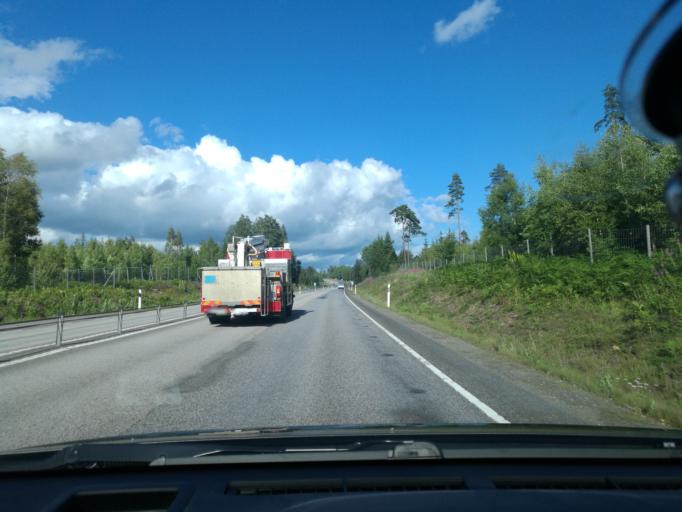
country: SE
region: Kronoberg
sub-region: Vaxjo Kommun
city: Braas
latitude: 56.9973
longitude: 15.0149
